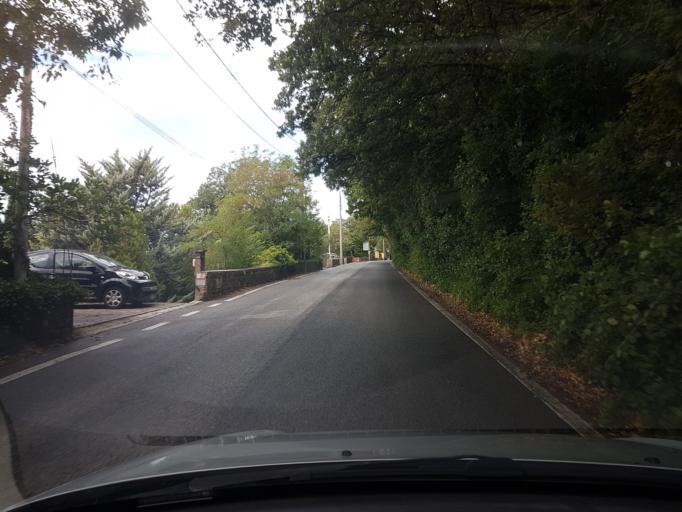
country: IT
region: Friuli Venezia Giulia
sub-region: Provincia di Trieste
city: Prosecco-Contovello
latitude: 45.6903
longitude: 13.7474
